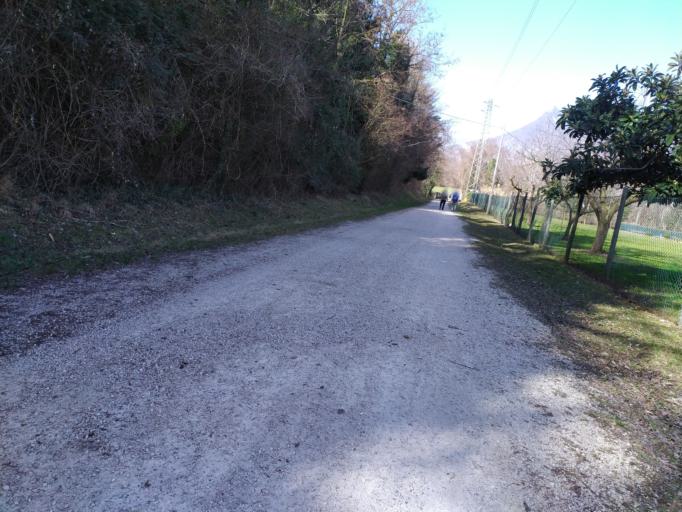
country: IT
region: Veneto
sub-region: Provincia di Vicenza
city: Velo d'Astico
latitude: 45.7856
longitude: 11.3870
